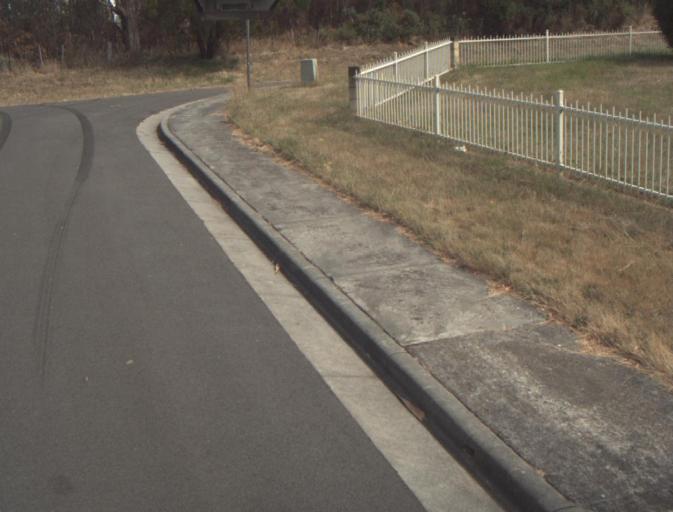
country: AU
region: Tasmania
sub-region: Launceston
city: Newstead
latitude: -41.4155
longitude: 147.1844
